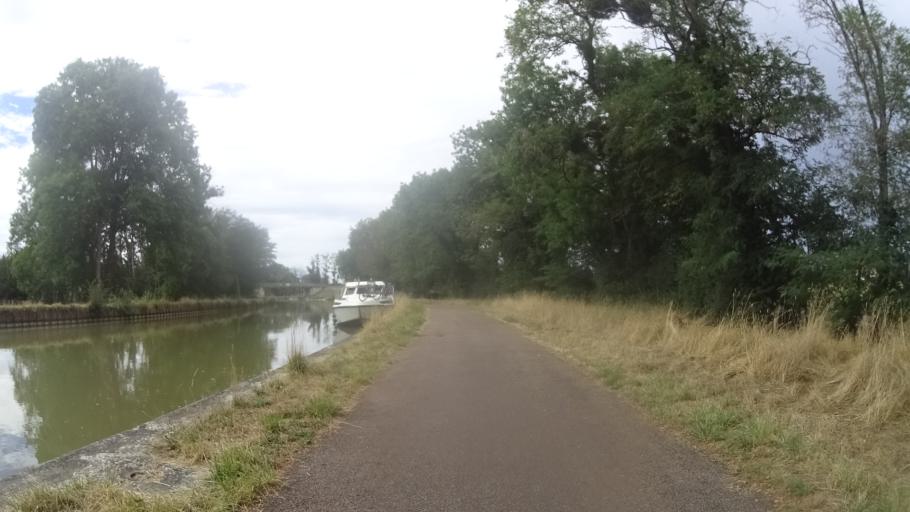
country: FR
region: Bourgogne
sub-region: Departement de la Nievre
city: Imphy
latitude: 46.9247
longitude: 3.2370
